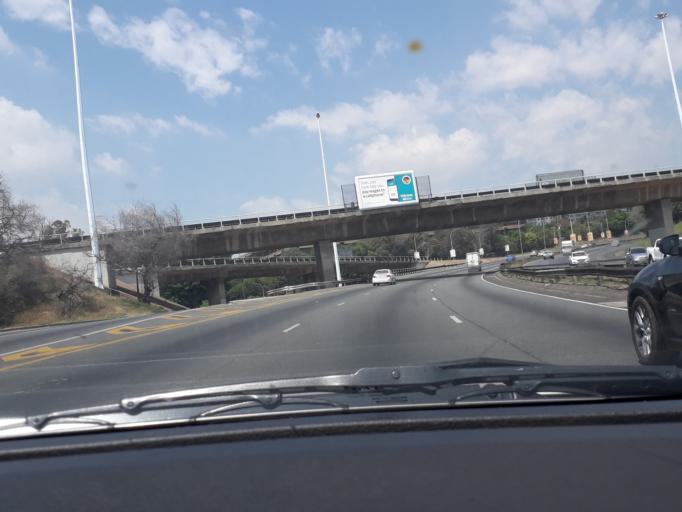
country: ZA
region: Gauteng
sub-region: City of Johannesburg Metropolitan Municipality
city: Johannesburg
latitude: -26.1675
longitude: 28.0549
